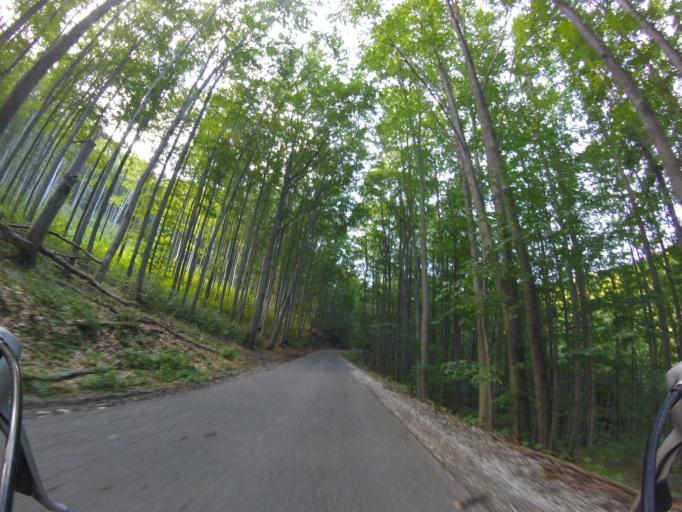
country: HU
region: Borsod-Abauj-Zemplen
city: Sajobabony
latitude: 48.1060
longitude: 20.6018
